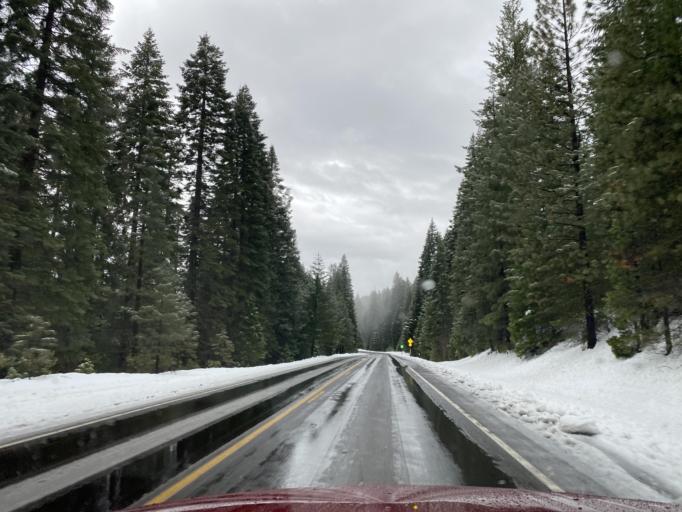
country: US
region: Oregon
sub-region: Klamath County
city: Klamath Falls
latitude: 42.5291
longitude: -122.0895
